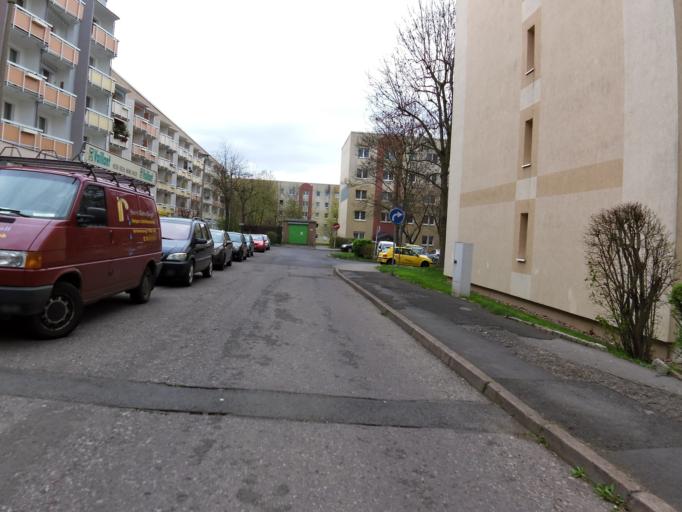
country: DE
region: Thuringia
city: Gotha
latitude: 50.9452
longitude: 10.6816
